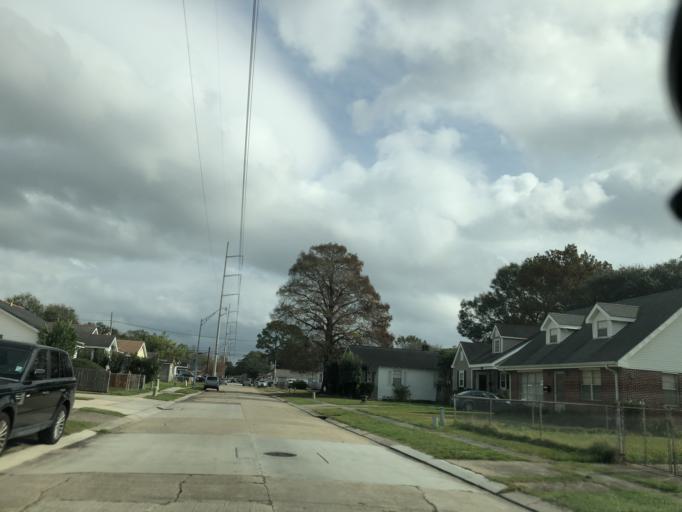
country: US
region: Louisiana
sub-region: Jefferson Parish
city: Metairie Terrace
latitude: 29.9769
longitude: -90.1684
